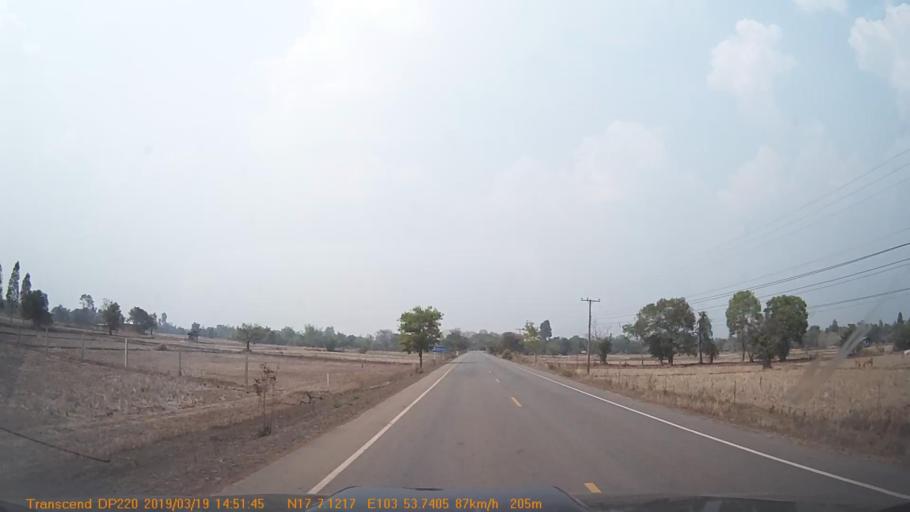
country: TH
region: Sakon Nakhon
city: Kut Bak
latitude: 17.1190
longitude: 103.8956
